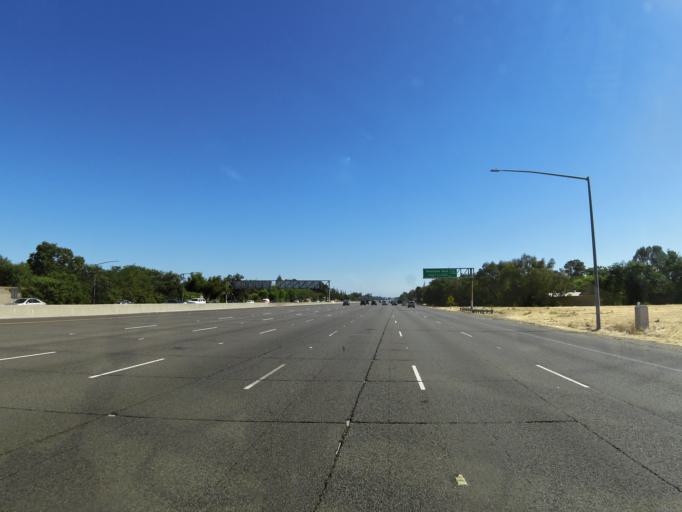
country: US
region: California
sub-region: Sacramento County
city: North Highlands
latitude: 38.6486
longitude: -121.3732
